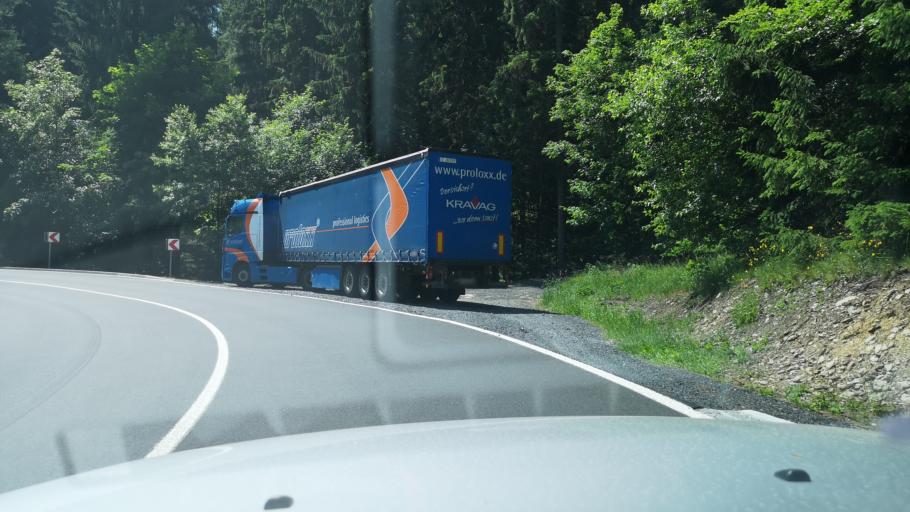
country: DE
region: Thuringia
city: Piesau
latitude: 50.5047
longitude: 11.2321
